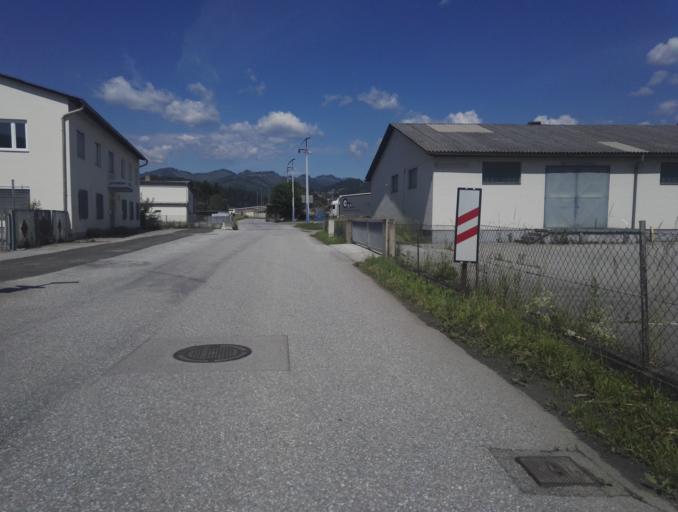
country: AT
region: Styria
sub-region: Politischer Bezirk Graz-Umgebung
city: Gratkorn
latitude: 47.1254
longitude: 15.3349
